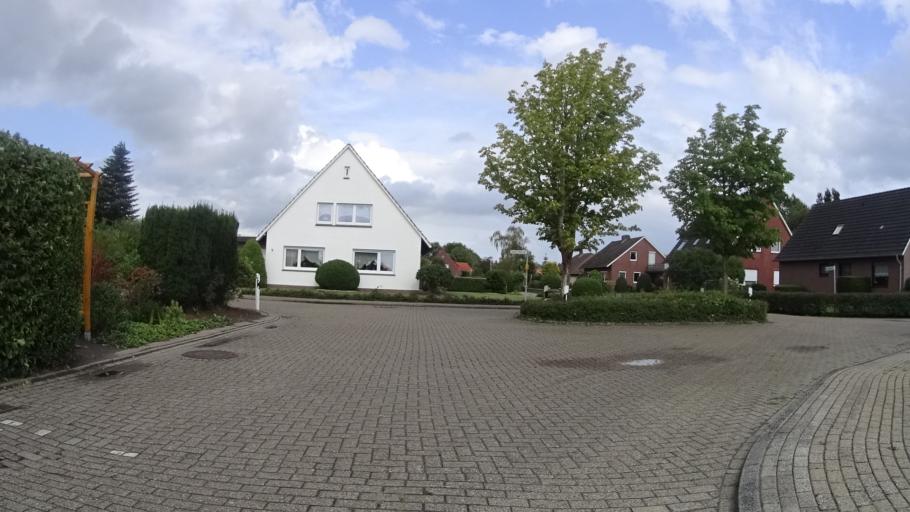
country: DE
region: Lower Saxony
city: Zetel
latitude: 53.3889
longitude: 7.9591
